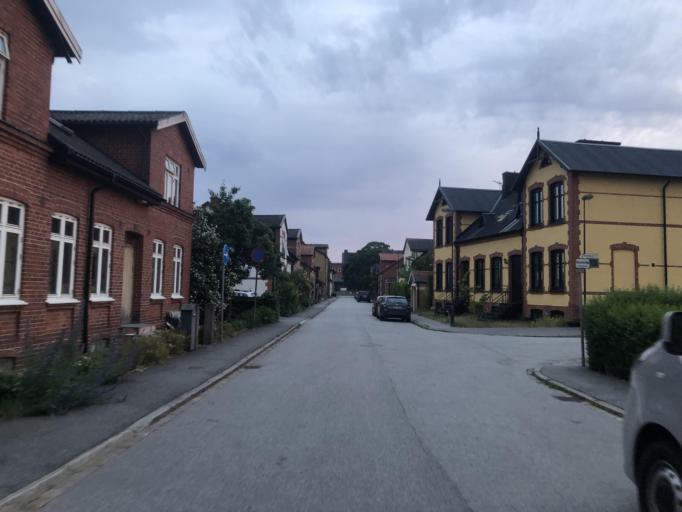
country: SE
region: Skane
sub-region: Malmo
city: Malmoe
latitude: 55.5972
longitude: 13.0414
